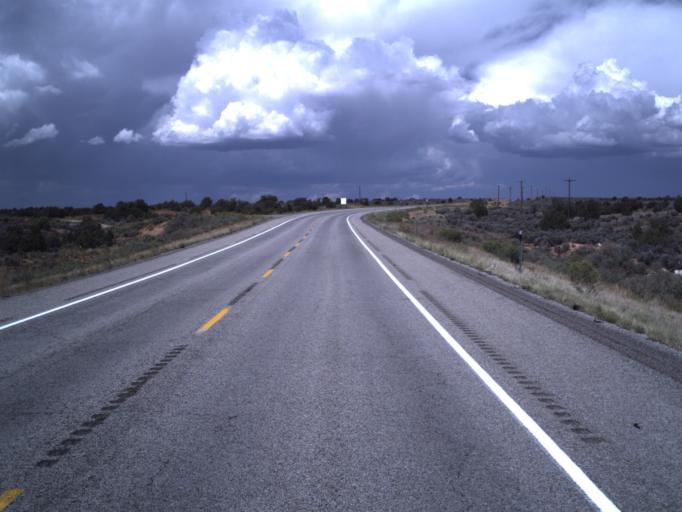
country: US
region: Utah
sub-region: San Juan County
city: Blanding
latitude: 37.4884
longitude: -109.4771
